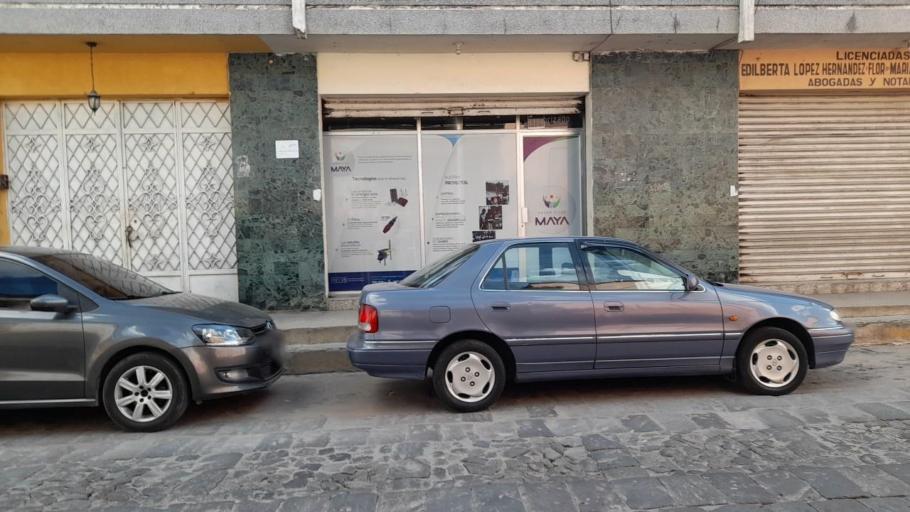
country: GT
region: Quetzaltenango
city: Quetzaltenango
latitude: 14.8321
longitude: -91.5165
